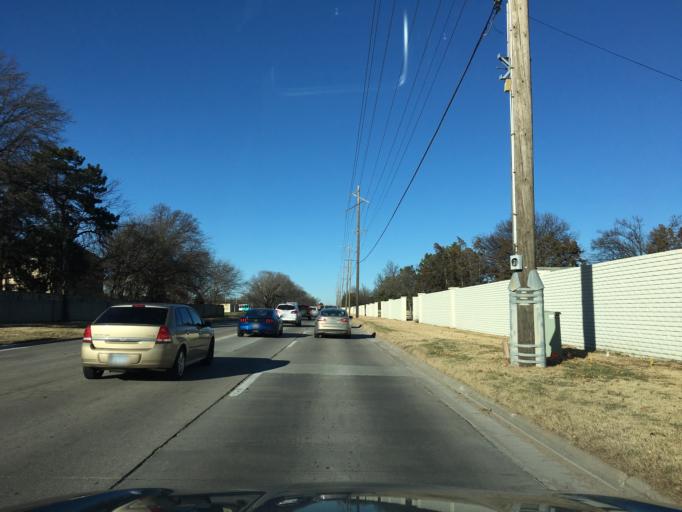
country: US
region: Kansas
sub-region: Sedgwick County
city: Bellaire
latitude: 37.7016
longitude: -97.2446
